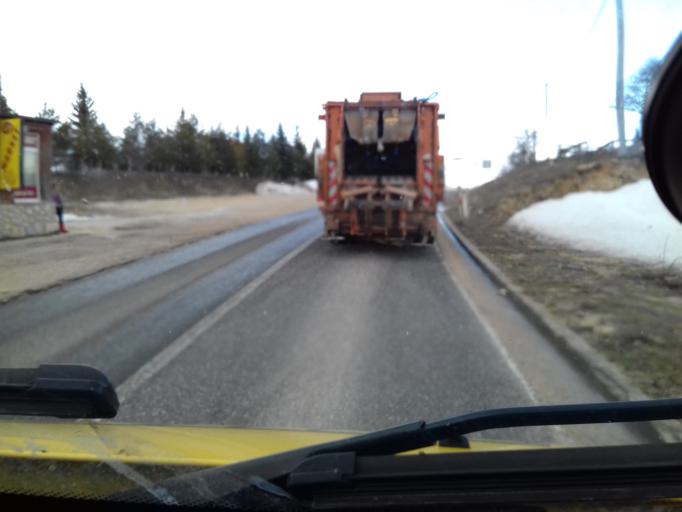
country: BA
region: Federation of Bosnia and Herzegovina
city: Tomislavgrad
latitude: 43.7315
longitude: 17.2221
